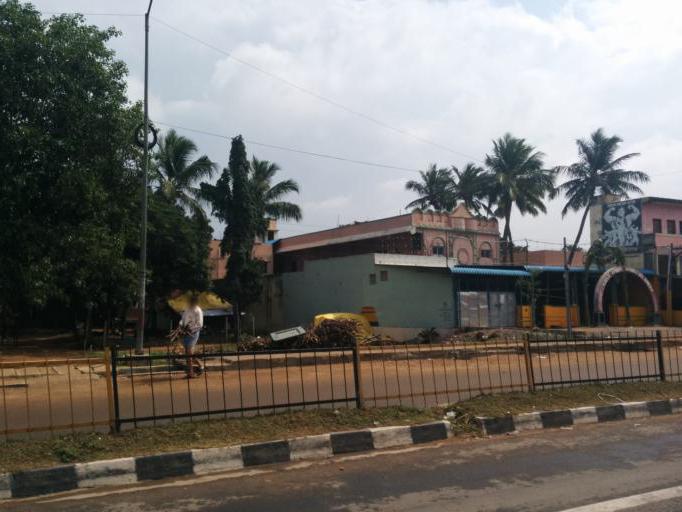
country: IN
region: Tamil Nadu
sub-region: Kancheepuram
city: Singapperumalkovil
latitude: 12.7572
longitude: 80.0025
